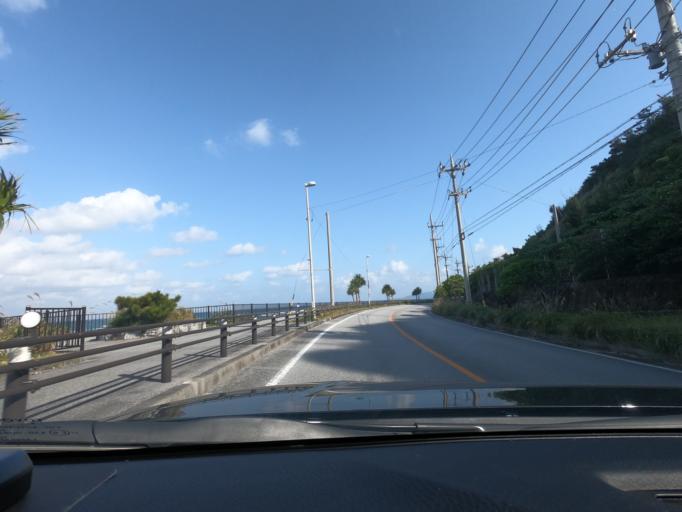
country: JP
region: Okinawa
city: Nago
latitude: 26.7604
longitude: 128.1896
